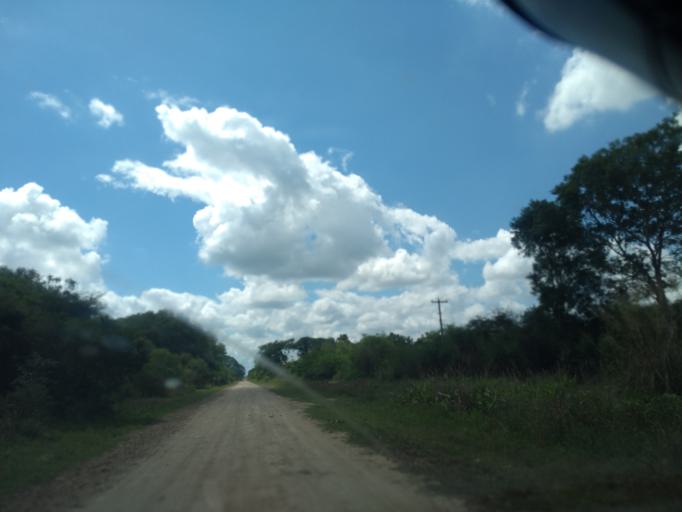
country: AR
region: Chaco
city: Fontana
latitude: -27.4264
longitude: -59.0610
